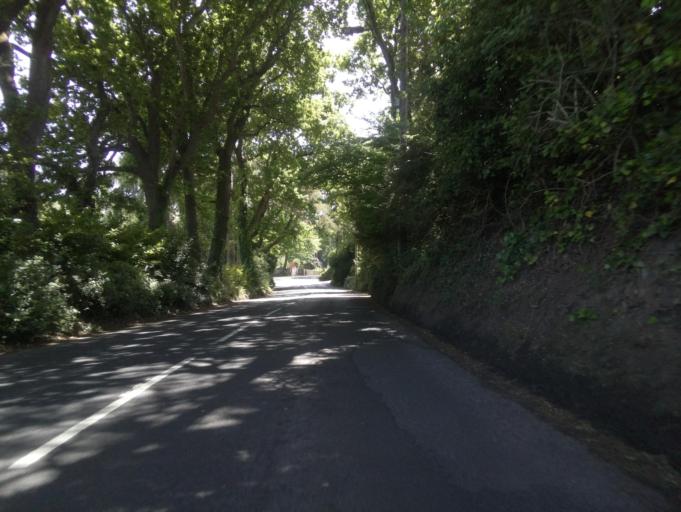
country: GB
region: England
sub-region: Devon
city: Budleigh Salterton
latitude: 50.6317
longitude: -3.3419
